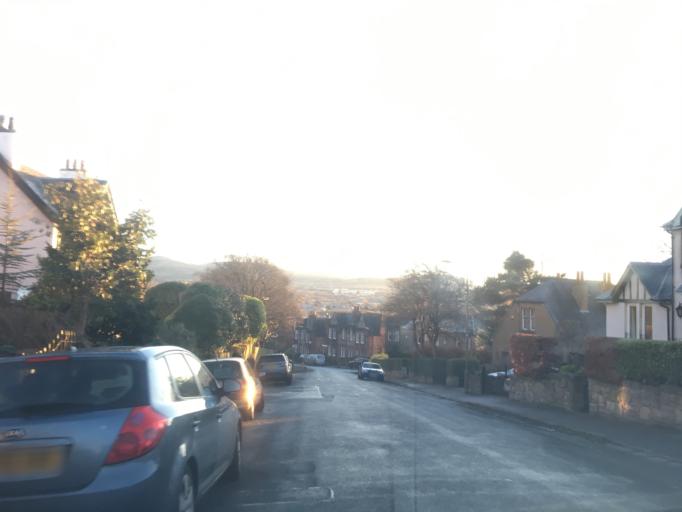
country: GB
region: Scotland
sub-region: Edinburgh
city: Colinton
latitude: 55.9442
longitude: -3.2737
